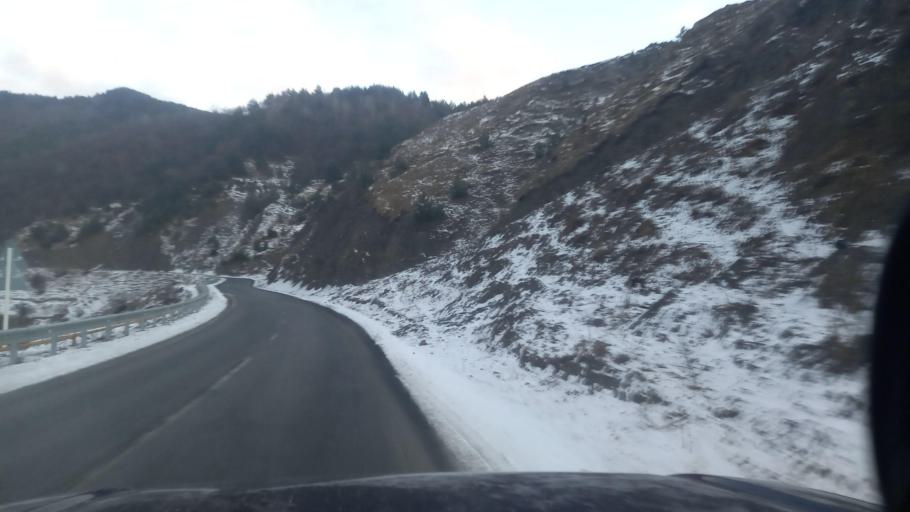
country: RU
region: Ingushetiya
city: Dzhayrakh
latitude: 42.8115
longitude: 44.8014
